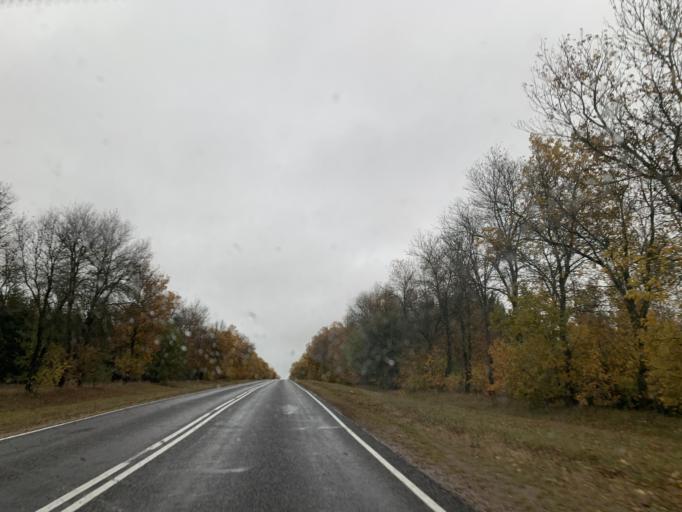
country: BY
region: Minsk
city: Novy Svyerzhan'
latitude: 53.4332
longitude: 26.6463
